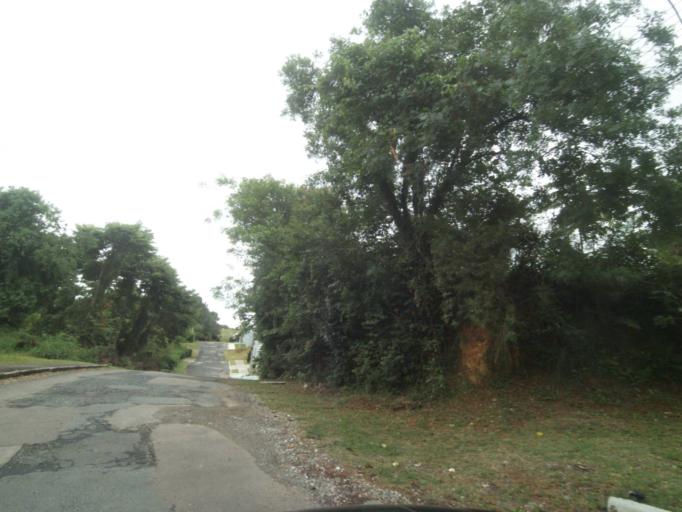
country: BR
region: Parana
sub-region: Curitiba
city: Curitiba
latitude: -25.4667
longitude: -49.3294
